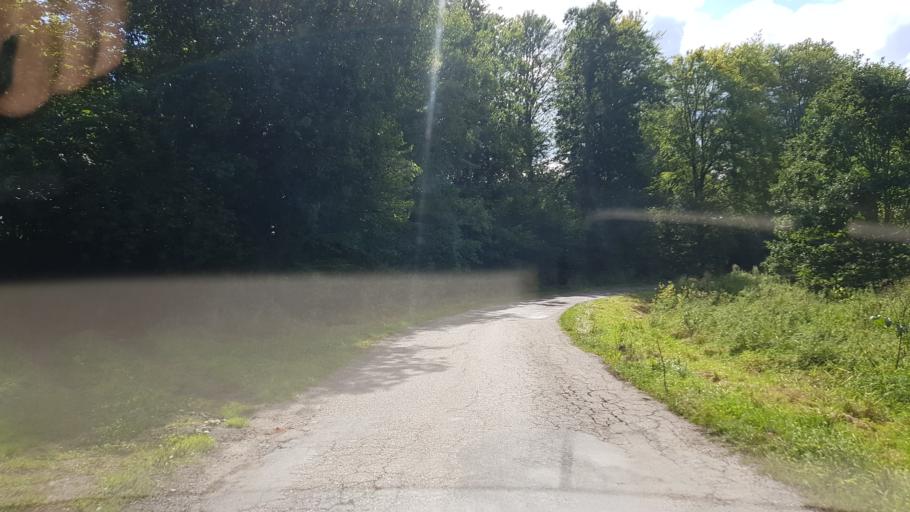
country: PL
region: West Pomeranian Voivodeship
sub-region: Powiat bialogardzki
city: Tychowo
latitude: 53.9904
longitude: 16.3029
